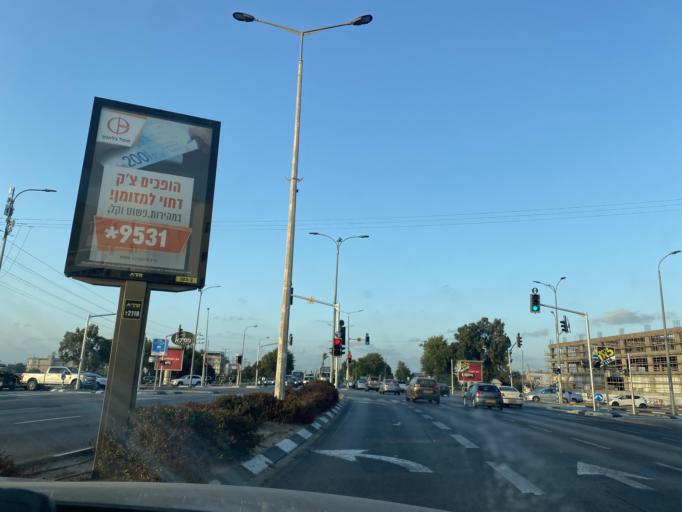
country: IL
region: Southern District
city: Ashdod
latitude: 31.8069
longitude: 34.6629
